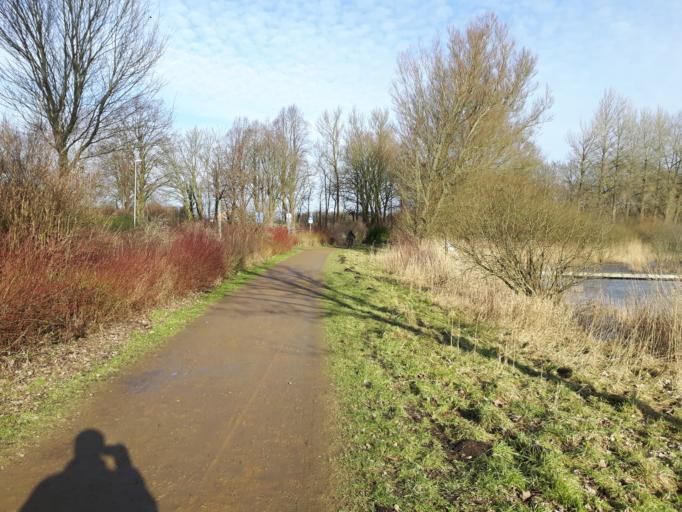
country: DE
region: Schleswig-Holstein
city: Muhbrook
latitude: 54.1353
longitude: 9.9874
